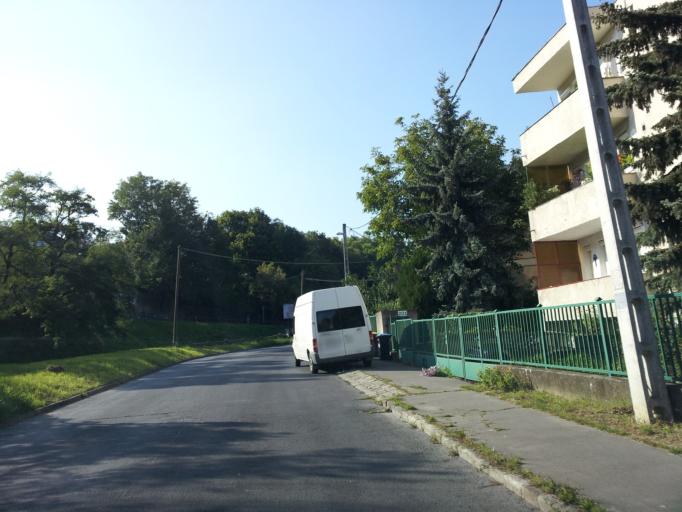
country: HU
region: Budapest
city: Budapest XII. keruelet
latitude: 47.5284
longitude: 18.9848
